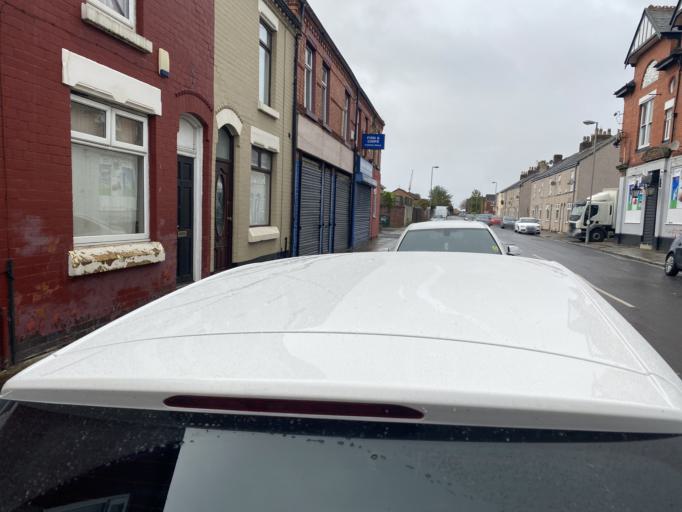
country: GB
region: England
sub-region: Liverpool
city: Liverpool
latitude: 53.4142
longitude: -2.9503
